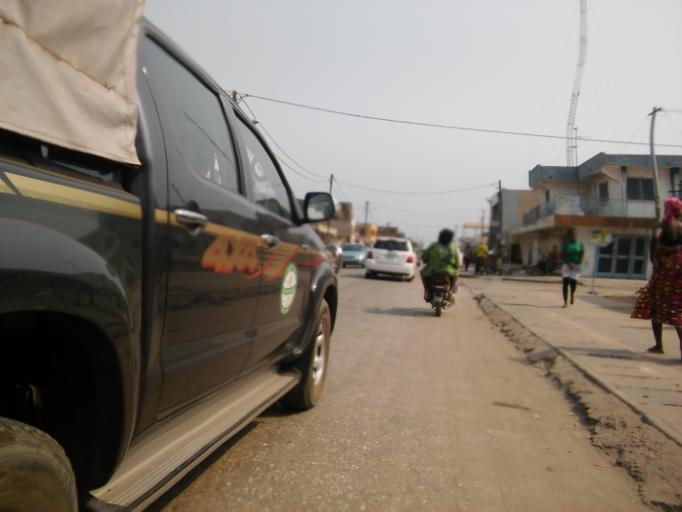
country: BJ
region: Littoral
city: Cotonou
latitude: 6.3759
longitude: 2.4129
